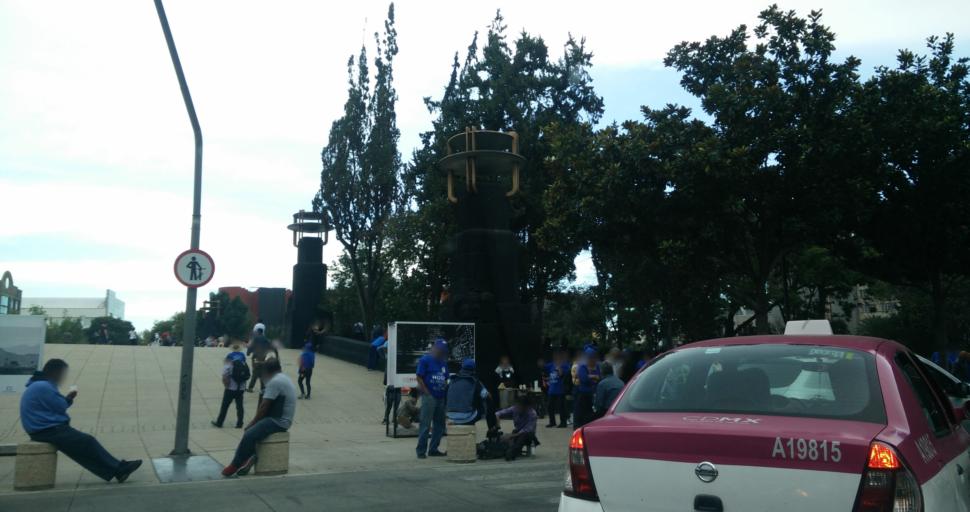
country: MX
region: Mexico City
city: Cuauhtemoc
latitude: 19.4355
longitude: -99.1543
